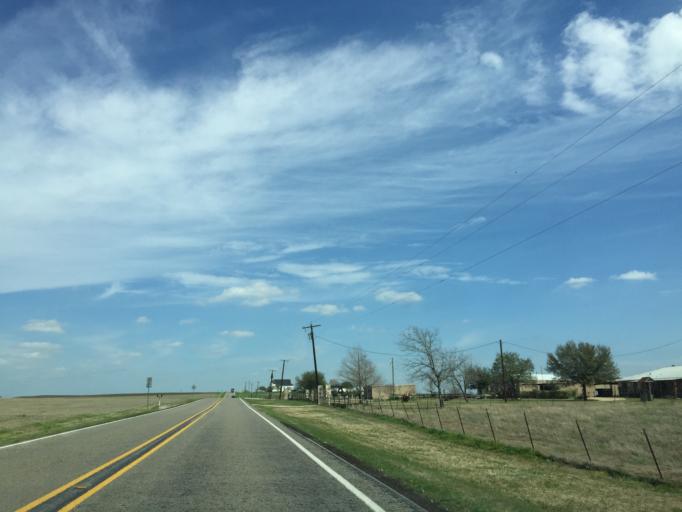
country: US
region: Texas
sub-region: Williamson County
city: Taylor
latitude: 30.5540
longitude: -97.3206
